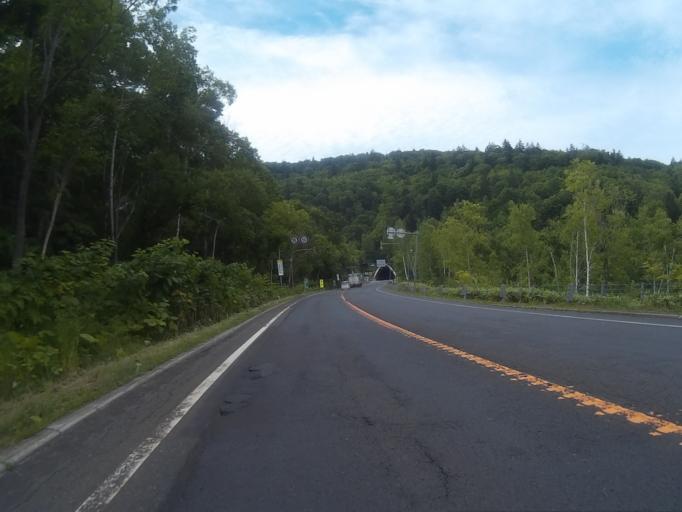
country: JP
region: Hokkaido
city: Sapporo
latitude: 42.8871
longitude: 141.1407
